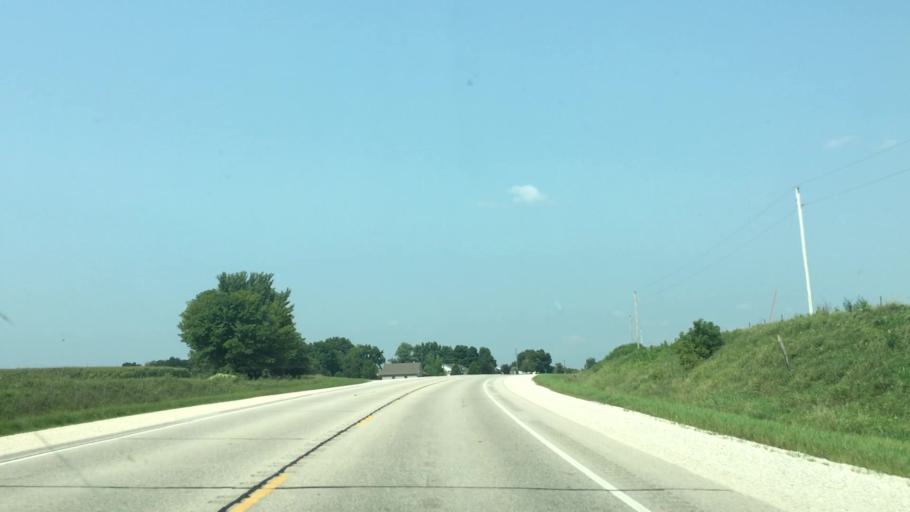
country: US
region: Iowa
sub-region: Winneshiek County
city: Decorah
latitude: 43.2606
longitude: -91.8379
